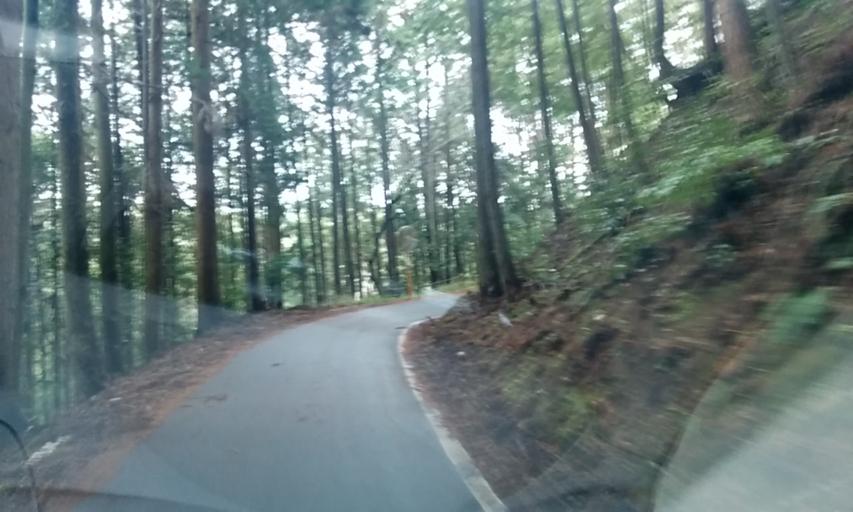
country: JP
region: Kyoto
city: Kameoka
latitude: 35.1143
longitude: 135.4294
